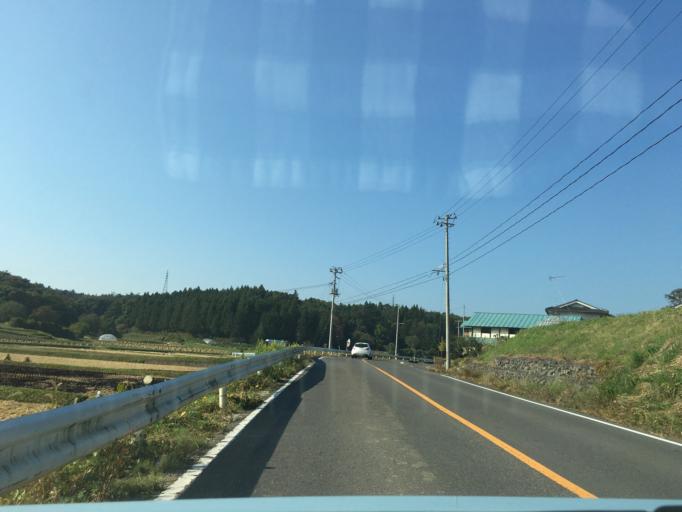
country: JP
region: Fukushima
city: Sukagawa
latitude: 37.2796
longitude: 140.3042
